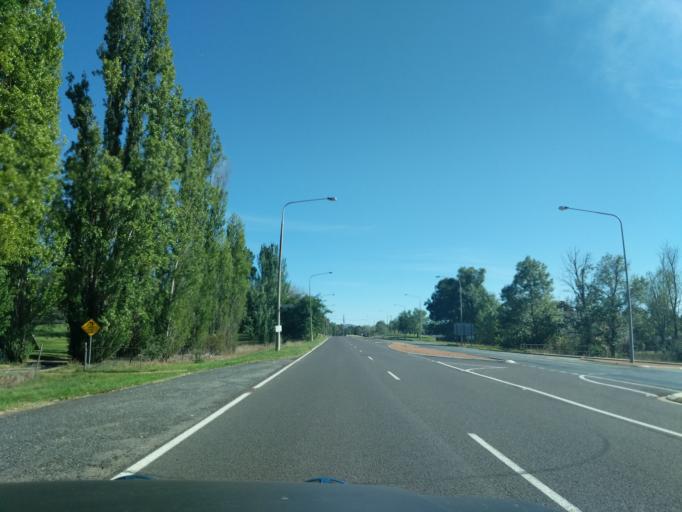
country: AU
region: Australian Capital Territory
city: Forrest
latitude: -35.3418
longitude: 149.1531
